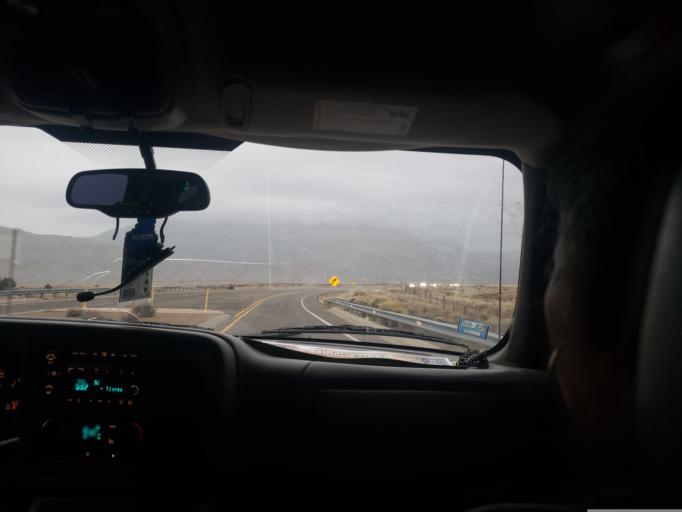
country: US
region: New Mexico
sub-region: Sandoval County
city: Corrales
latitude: 35.2022
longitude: -106.5573
